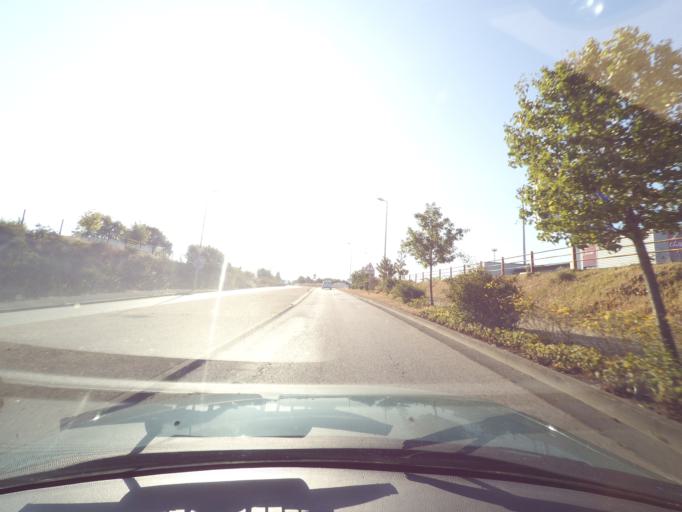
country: FR
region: Poitou-Charentes
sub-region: Departement des Deux-Sevres
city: Chatillon-sur-Thouet
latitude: 46.6543
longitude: -0.2370
